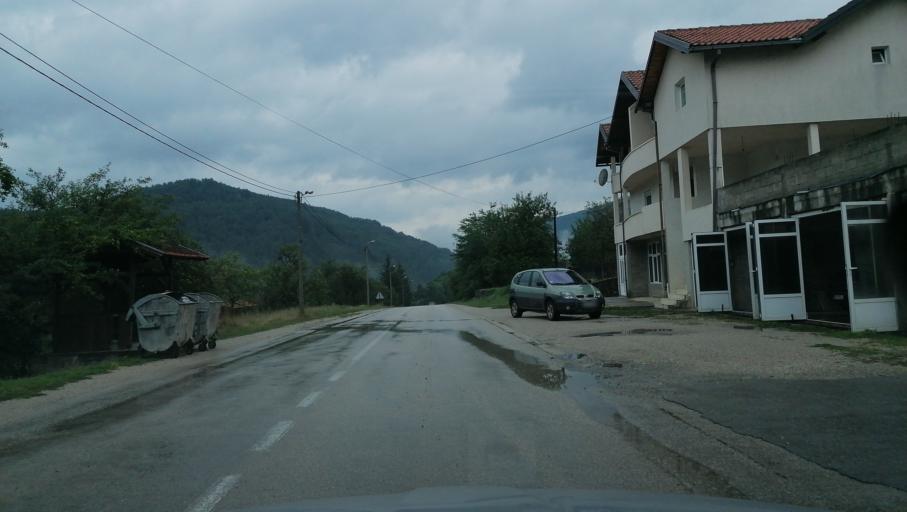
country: RS
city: Durici
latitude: 43.7912
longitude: 19.5077
